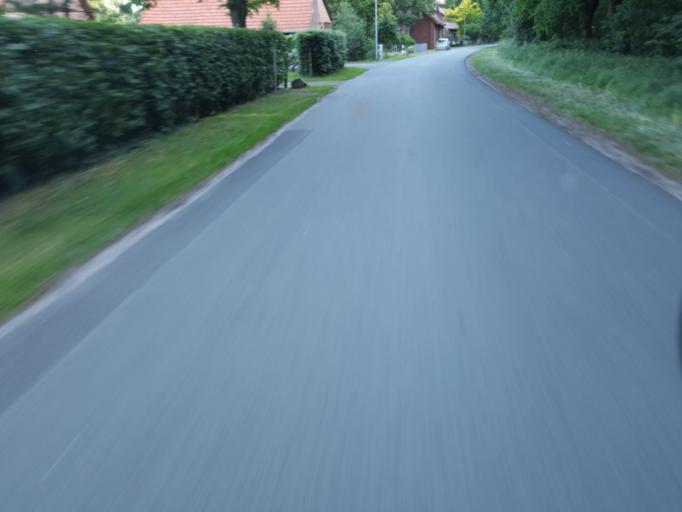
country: DE
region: Lower Saxony
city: Leese
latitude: 52.5297
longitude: 9.1243
